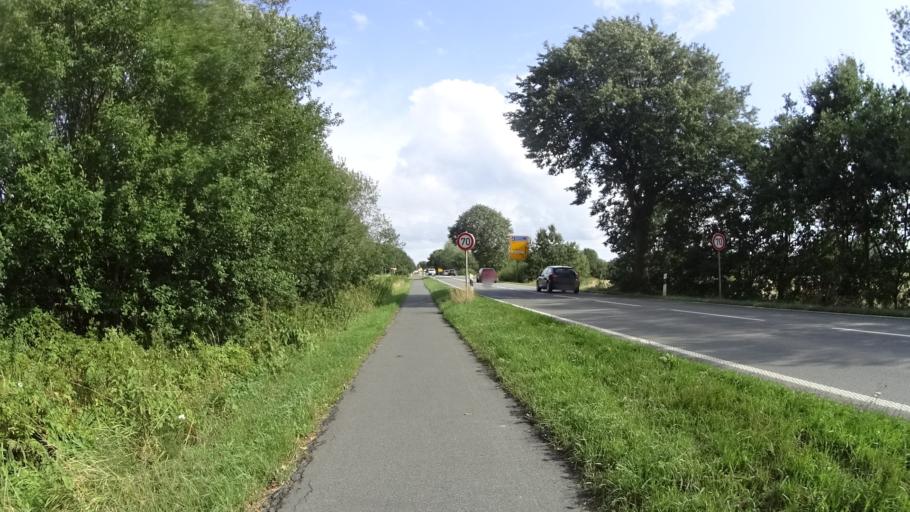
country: DE
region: Lower Saxony
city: Bockhorn
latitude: 53.3900
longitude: 8.0038
